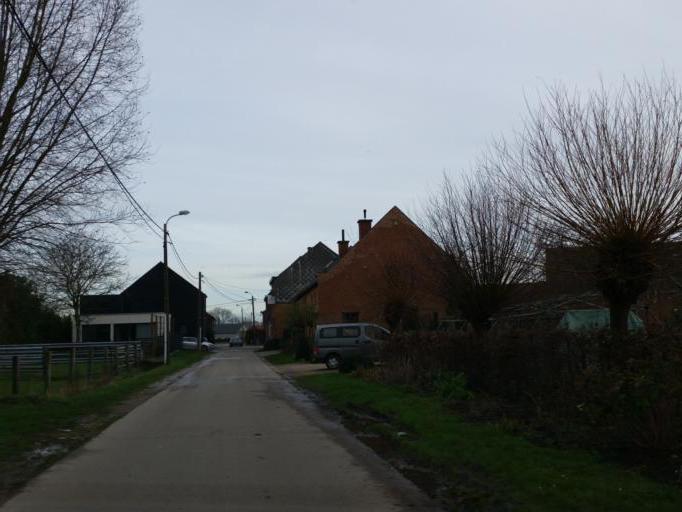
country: BE
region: Flanders
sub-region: Provincie Vlaams-Brabant
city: Zemst
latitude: 51.0052
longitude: 4.4158
